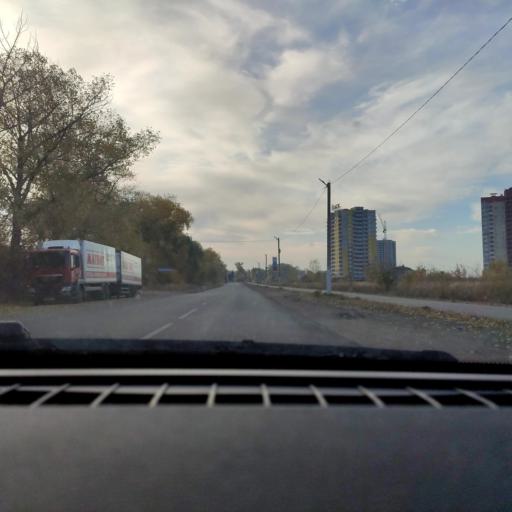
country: RU
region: Voronezj
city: Somovo
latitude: 51.6745
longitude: 39.3219
